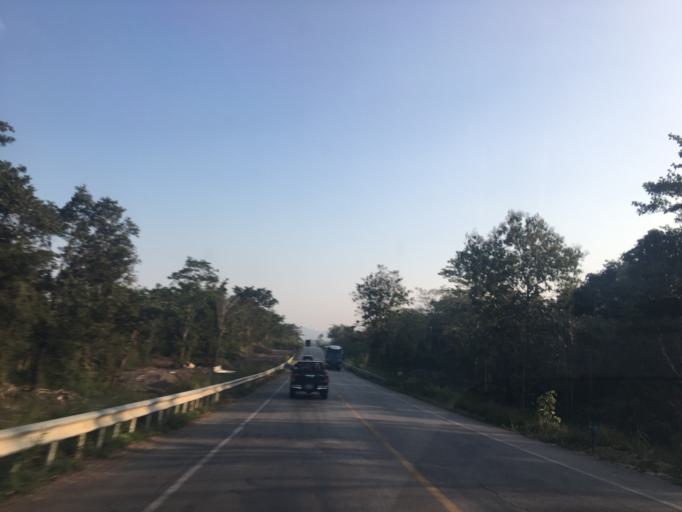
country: TH
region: Lampang
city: Ngao
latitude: 18.6974
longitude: 100.0015
